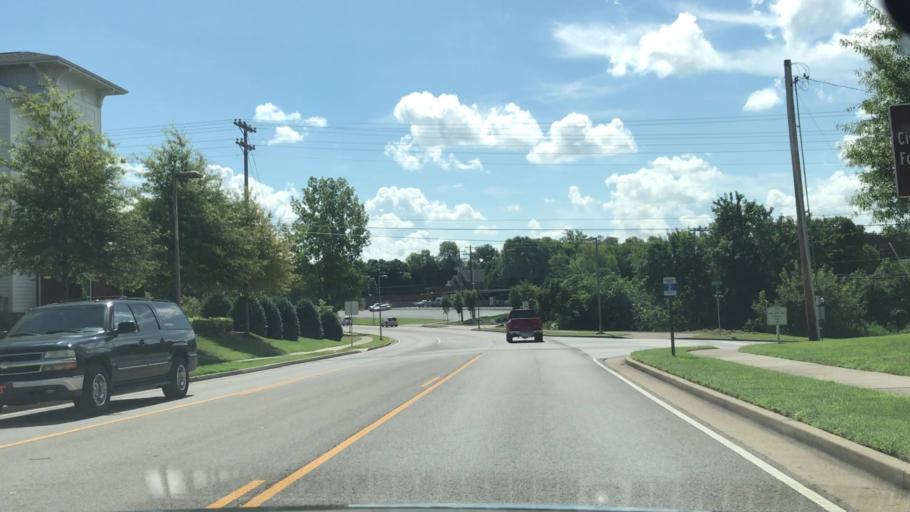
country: US
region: Tennessee
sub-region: Williamson County
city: Franklin
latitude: 35.9299
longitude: -86.8562
